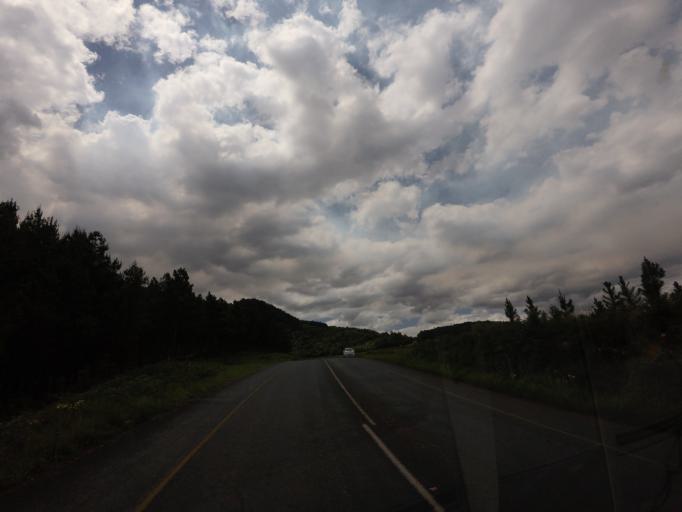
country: ZA
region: Mpumalanga
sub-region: Ehlanzeni District
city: Graksop
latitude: -24.9484
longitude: 30.8118
